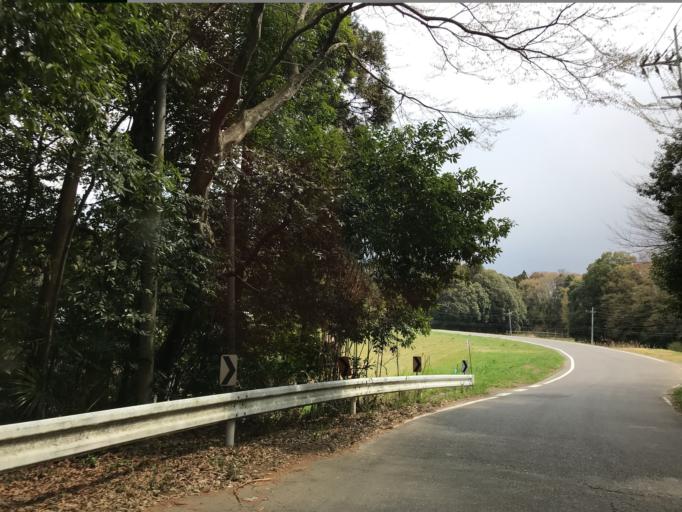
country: JP
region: Ibaraki
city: Moriya
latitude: 35.9559
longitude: 140.0102
